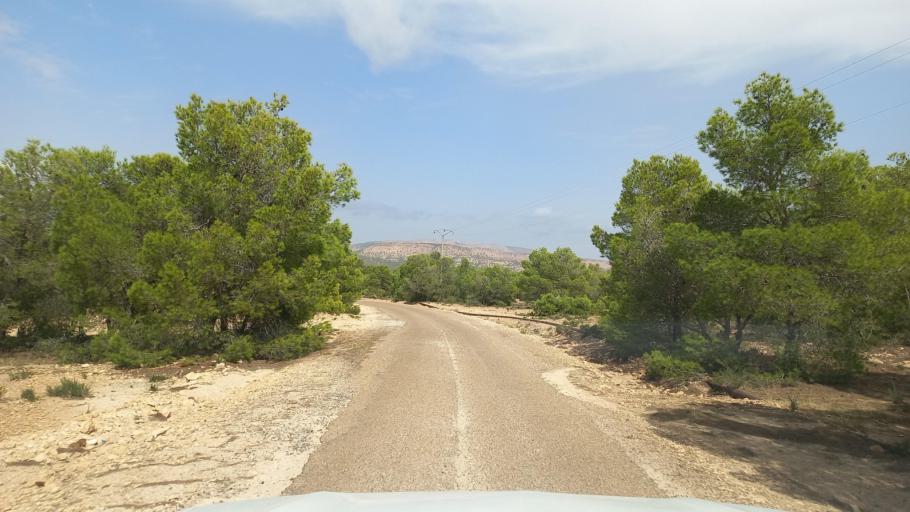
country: TN
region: Al Qasrayn
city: Sbiba
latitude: 35.3944
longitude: 8.9112
